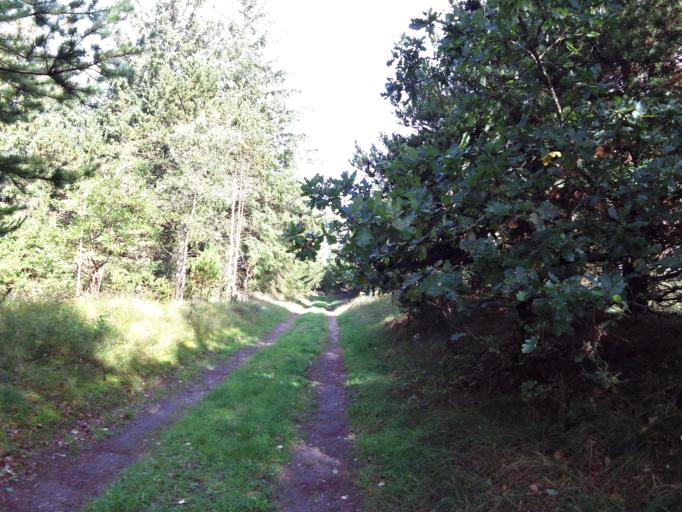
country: DK
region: South Denmark
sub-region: Varde Kommune
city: Oksbol
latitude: 55.5562
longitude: 8.2107
